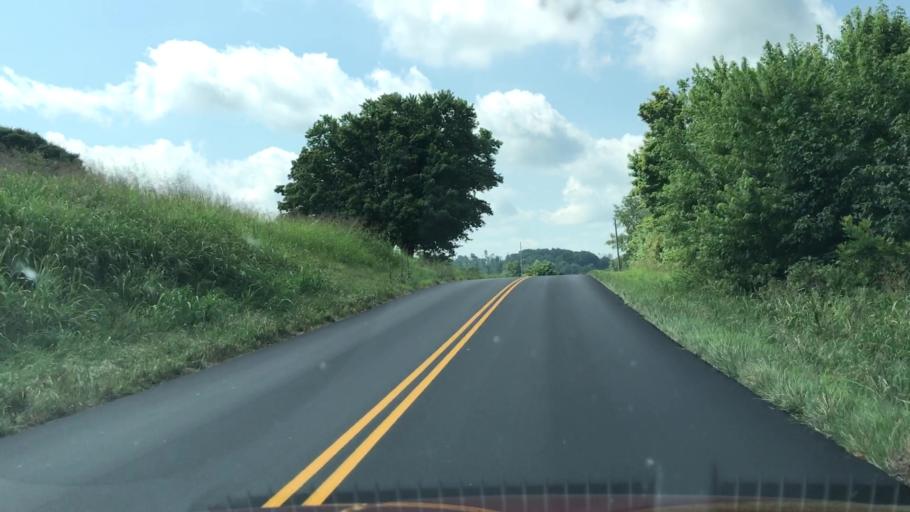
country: US
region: Kentucky
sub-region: Monroe County
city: Tompkinsville
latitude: 36.7717
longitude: -85.7990
